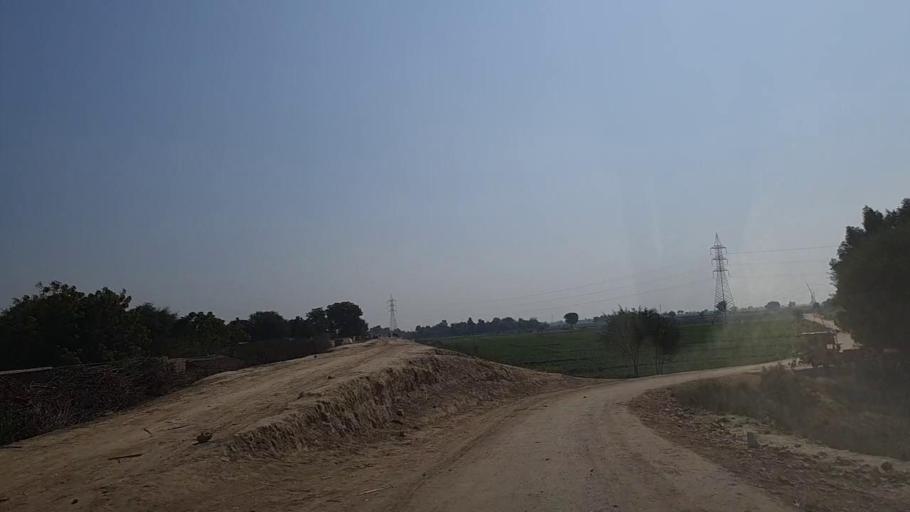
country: PK
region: Sindh
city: Moro
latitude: 26.7027
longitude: 67.9267
